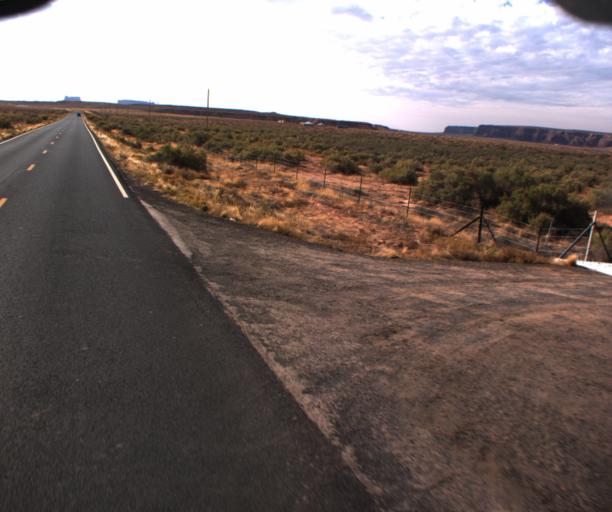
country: US
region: Arizona
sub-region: Apache County
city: Many Farms
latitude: 36.6254
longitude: -109.5832
